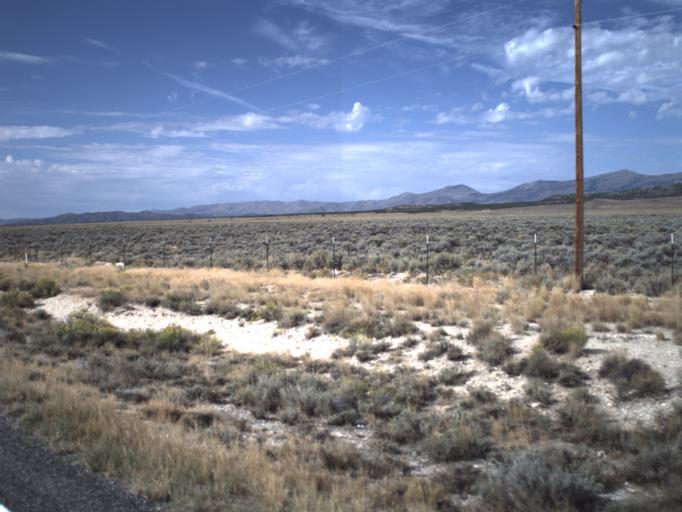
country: US
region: Idaho
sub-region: Cassia County
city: Burley
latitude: 41.7543
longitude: -113.5146
